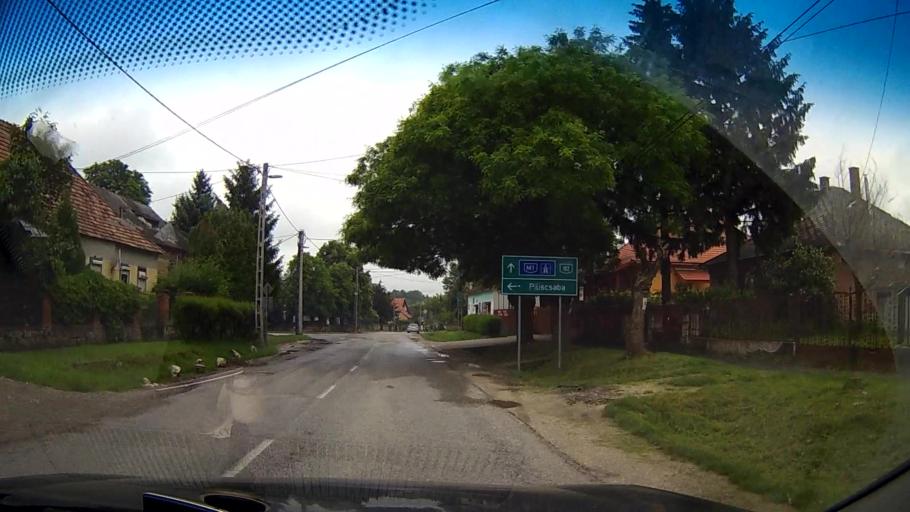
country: HU
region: Pest
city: Perbal
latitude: 47.6204
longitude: 18.7779
